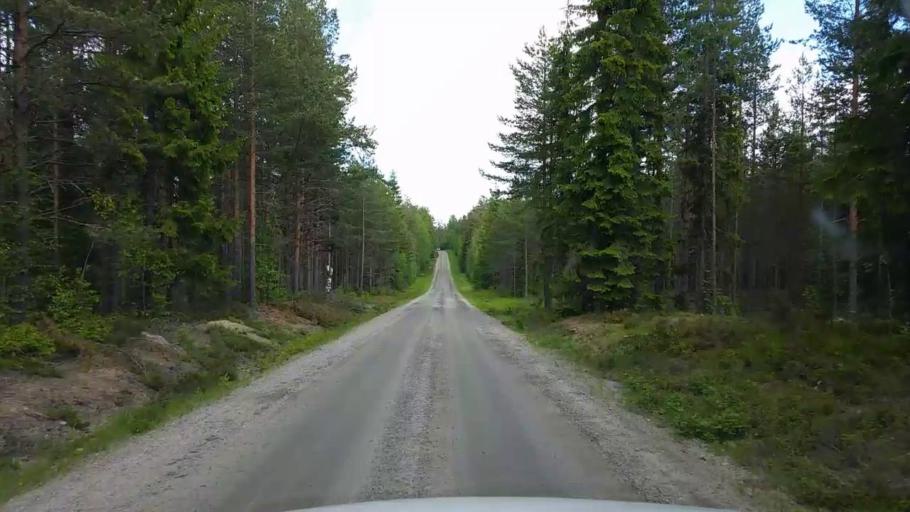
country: SE
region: Gaevleborg
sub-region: Ovanakers Kommun
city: Alfta
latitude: 61.5589
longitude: 15.9878
